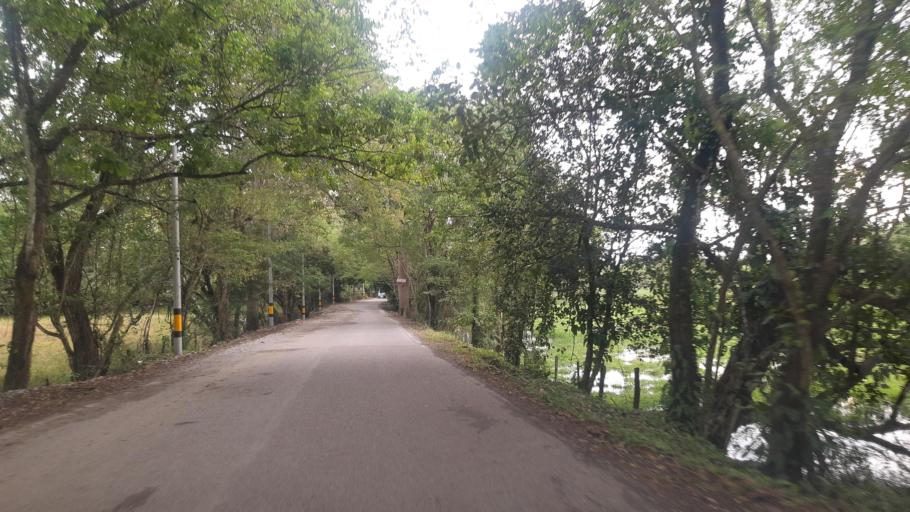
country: CO
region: Antioquia
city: Puerto Triunfo
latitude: 5.8815
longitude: -74.6337
